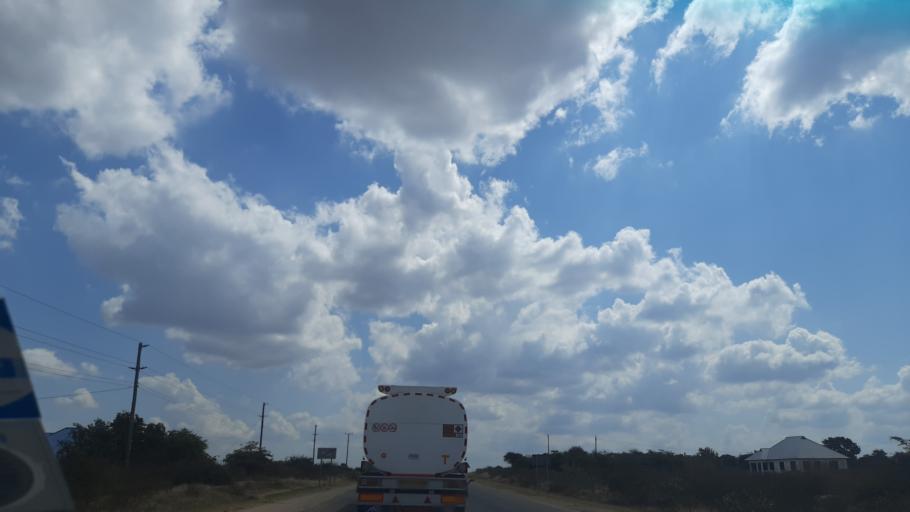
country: TZ
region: Dodoma
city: Dodoma
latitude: -6.0886
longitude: 35.6149
